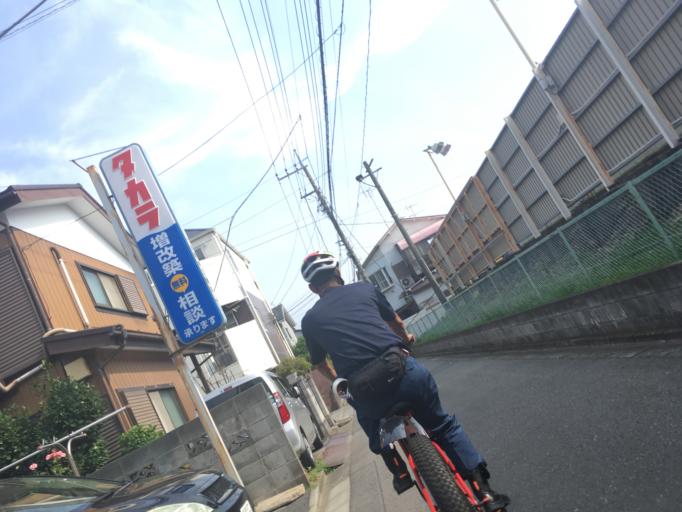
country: JP
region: Kanagawa
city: Minami-rinkan
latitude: 35.4703
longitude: 139.4652
